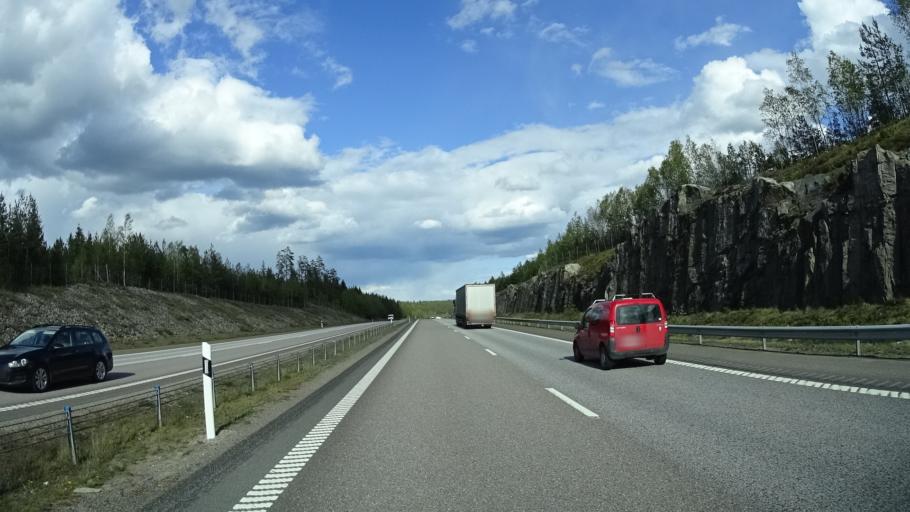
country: SE
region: OEstergoetland
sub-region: Norrkopings Kommun
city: Krokek
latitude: 58.7412
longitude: 16.4507
